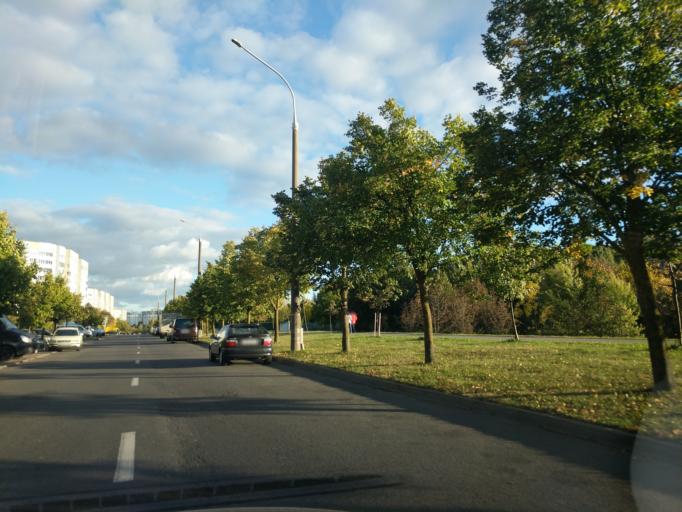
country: BY
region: Minsk
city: Malinovka
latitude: 53.8600
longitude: 27.4505
